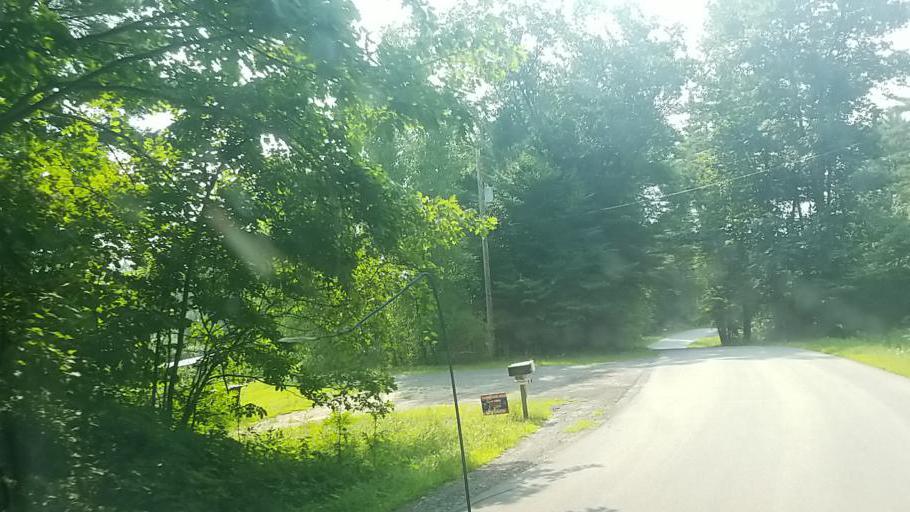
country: US
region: New York
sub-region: Montgomery County
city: Fonda
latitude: 42.9275
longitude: -74.4473
